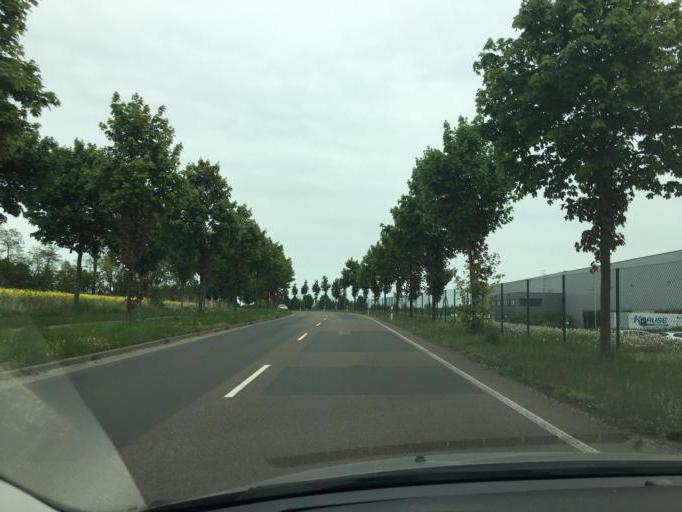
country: DE
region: Saxony
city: Taucha
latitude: 51.3962
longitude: 12.4335
